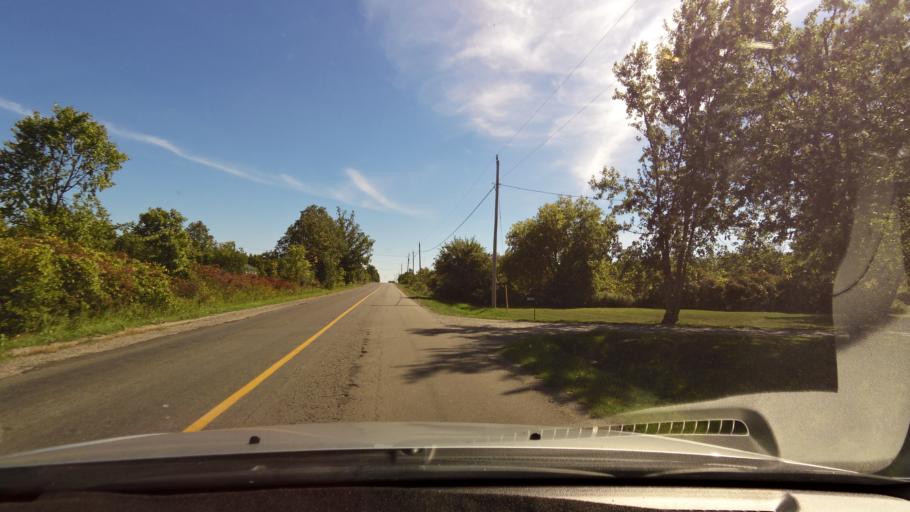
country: CA
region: Ontario
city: Ancaster
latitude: 43.0683
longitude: -80.0608
